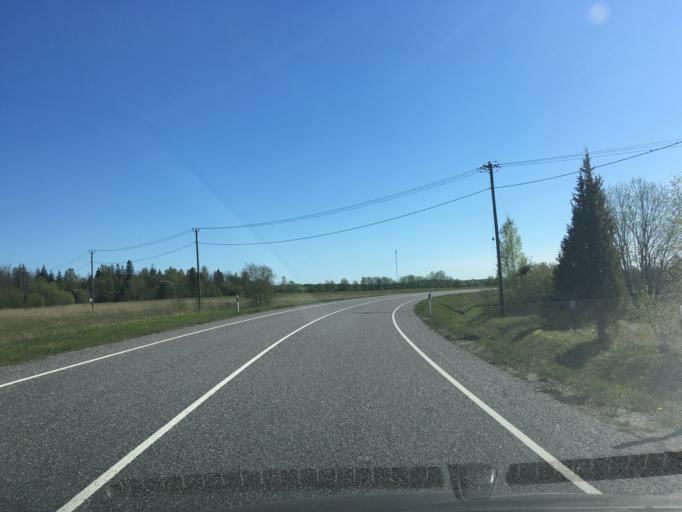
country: EE
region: Harju
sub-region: Rae vald
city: Vaida
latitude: 59.2629
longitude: 25.0220
